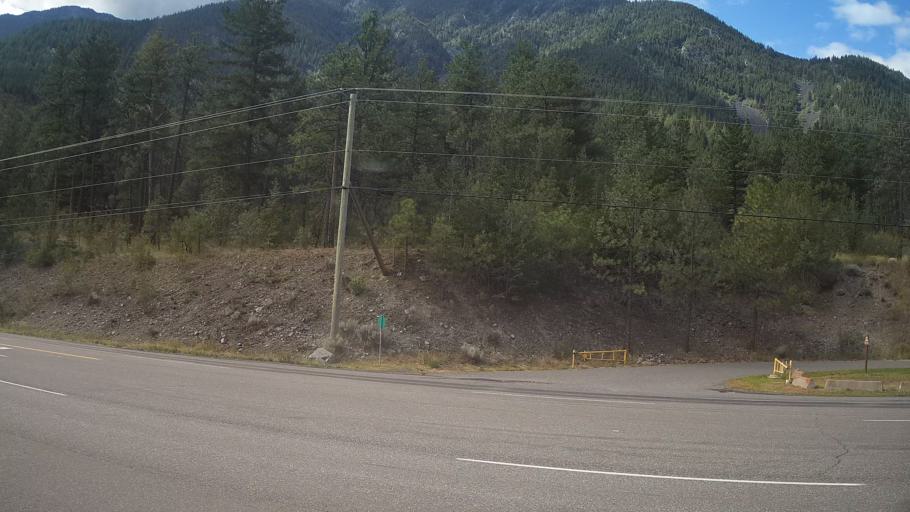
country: CA
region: British Columbia
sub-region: Thompson-Nicola Regional District
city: Ashcroft
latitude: 50.2532
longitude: -121.5077
